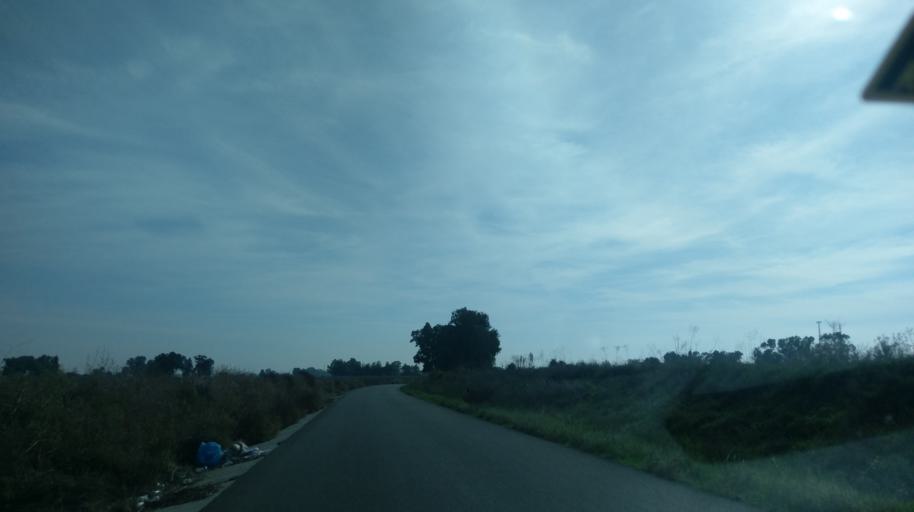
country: CY
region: Larnaka
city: Athienou
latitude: 35.1662
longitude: 33.6042
